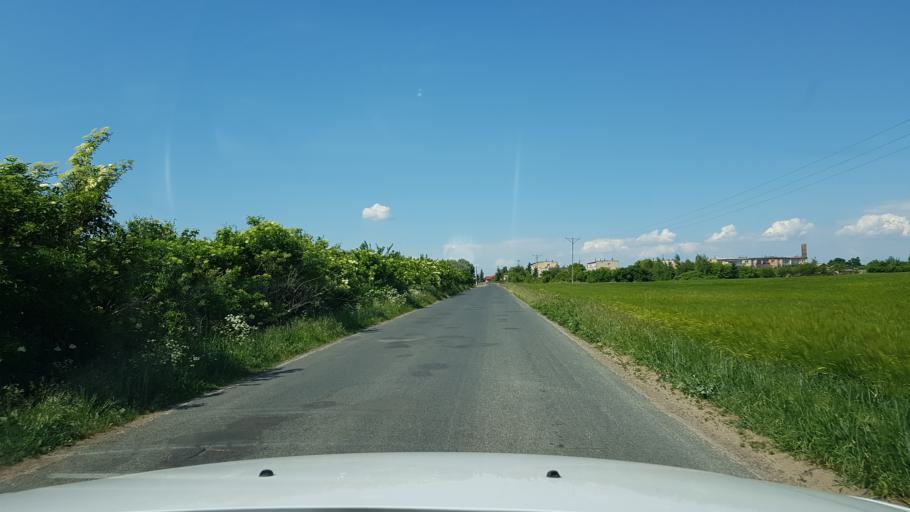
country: PL
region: West Pomeranian Voivodeship
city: Trzcinsko Zdroj
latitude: 53.0142
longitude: 14.5630
